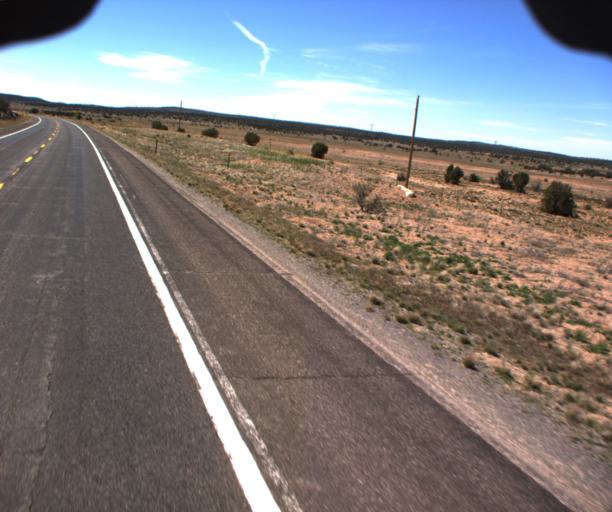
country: US
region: Arizona
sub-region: Mohave County
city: Peach Springs
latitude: 35.5536
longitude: -113.3191
